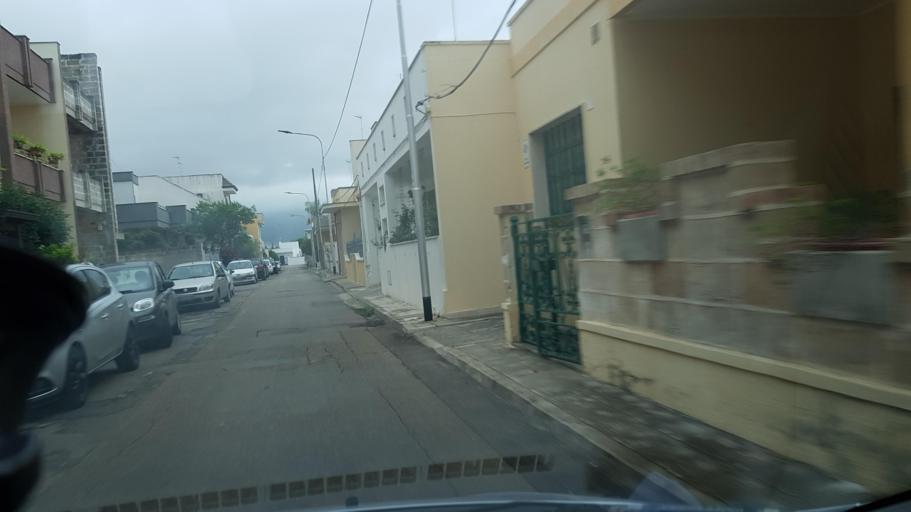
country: IT
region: Apulia
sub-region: Provincia di Lecce
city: Carmiano
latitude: 40.3510
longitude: 18.0392
